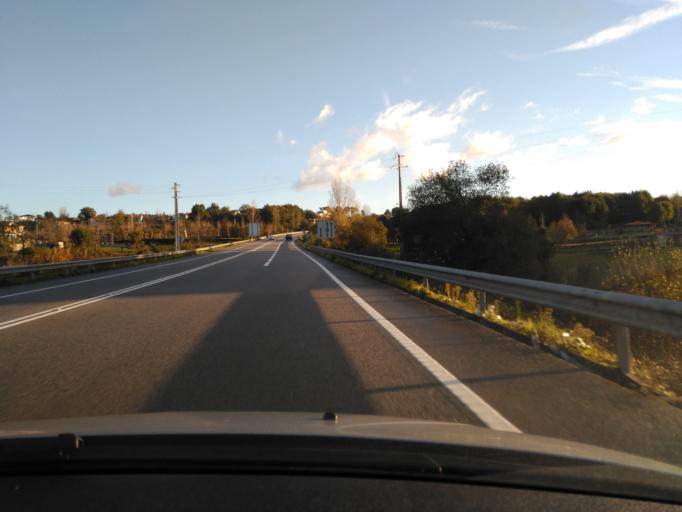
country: PT
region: Braga
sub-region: Fafe
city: Fafe
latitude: 41.4616
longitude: -8.1821
